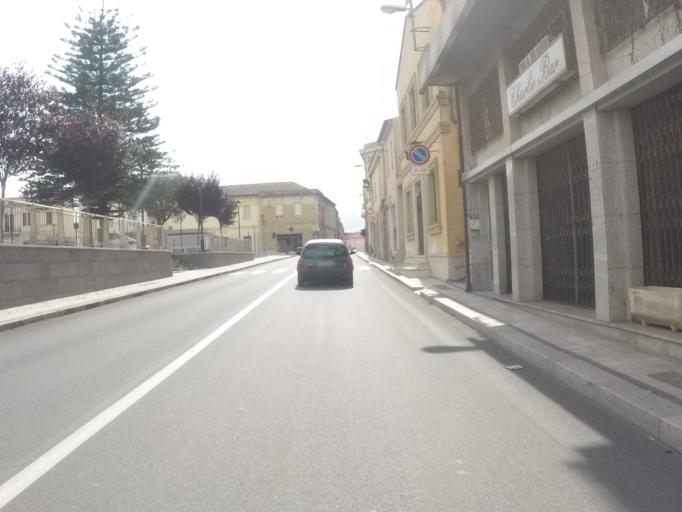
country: IT
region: Sardinia
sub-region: Provincia di Oristano
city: Terralba
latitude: 39.7207
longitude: 8.6371
